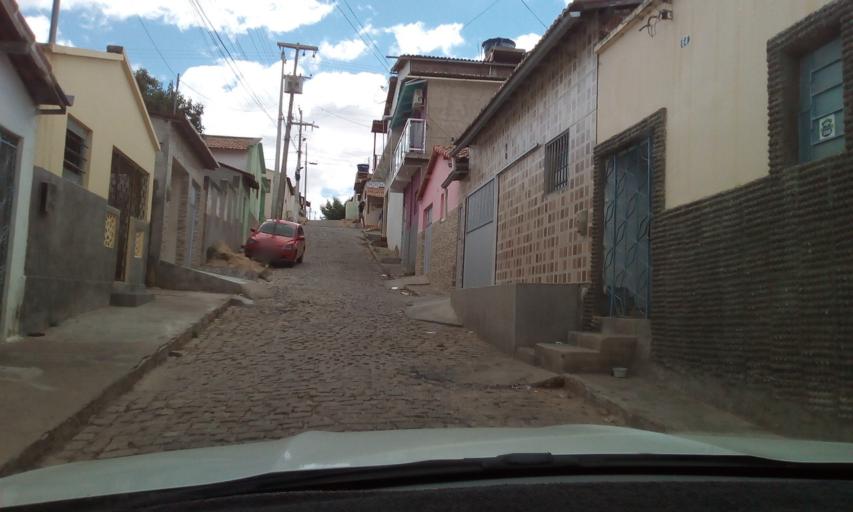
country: BR
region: Paraiba
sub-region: Picui
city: Picui
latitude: -6.5122
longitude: -36.3528
